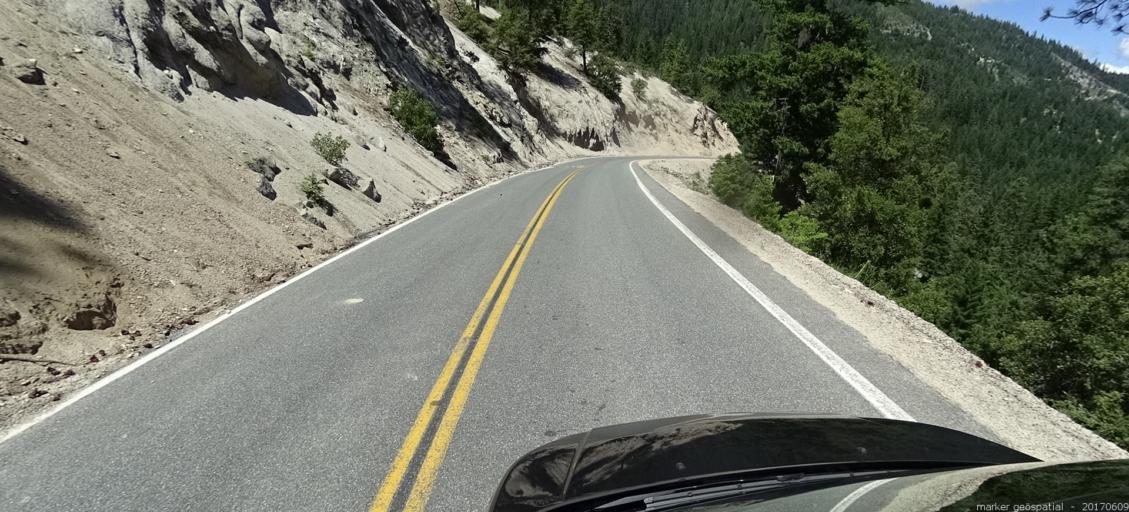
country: US
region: California
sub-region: Siskiyou County
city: Yreka
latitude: 41.4260
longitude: -122.9616
